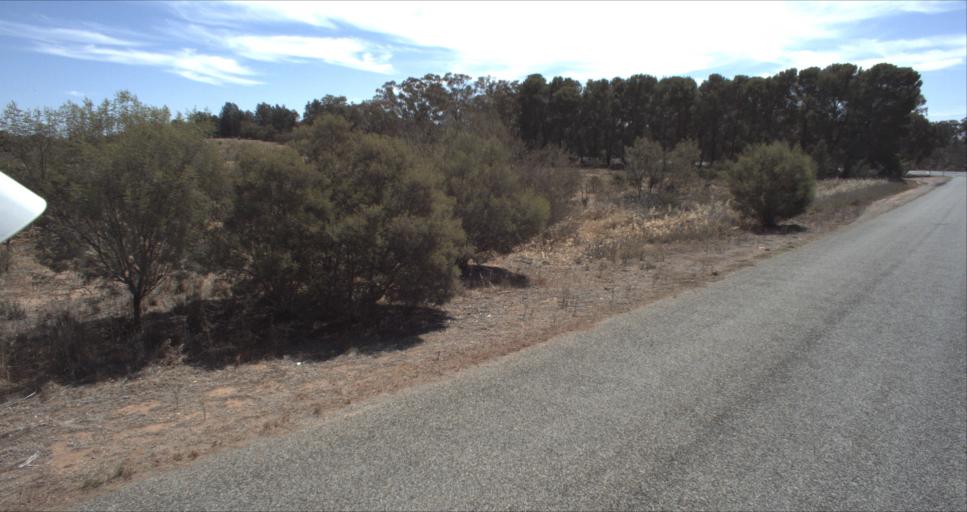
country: AU
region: New South Wales
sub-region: Leeton
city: Leeton
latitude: -34.6661
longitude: 146.4470
